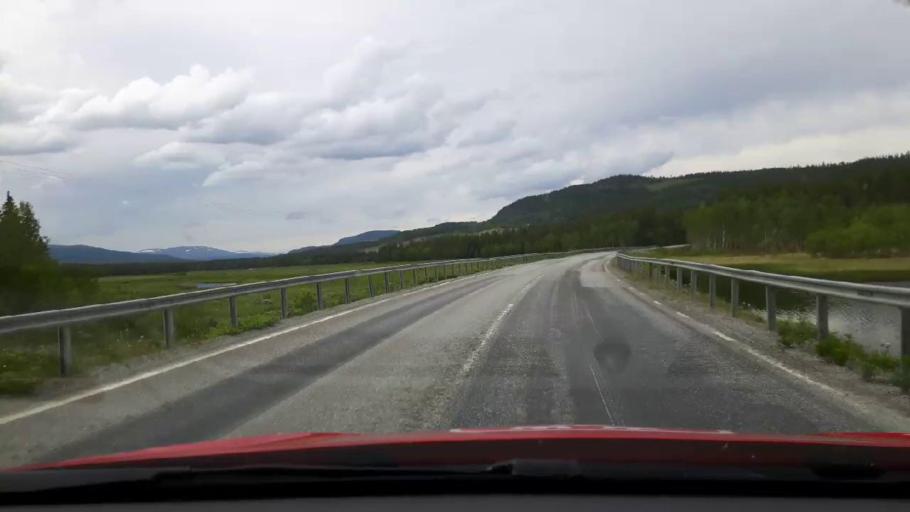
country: NO
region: Hedmark
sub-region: Engerdal
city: Engerdal
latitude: 62.4277
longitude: 12.7200
